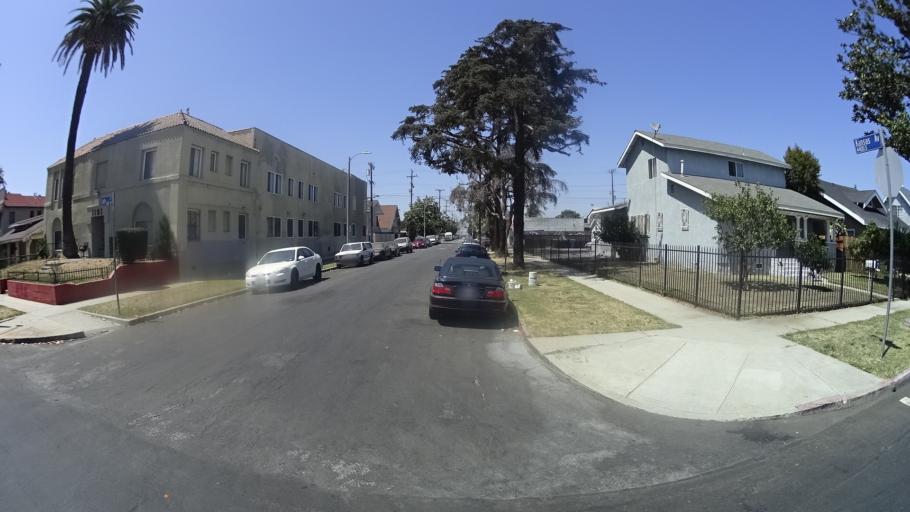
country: US
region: California
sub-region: Los Angeles County
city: View Park-Windsor Hills
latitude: 34.0027
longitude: -118.2937
